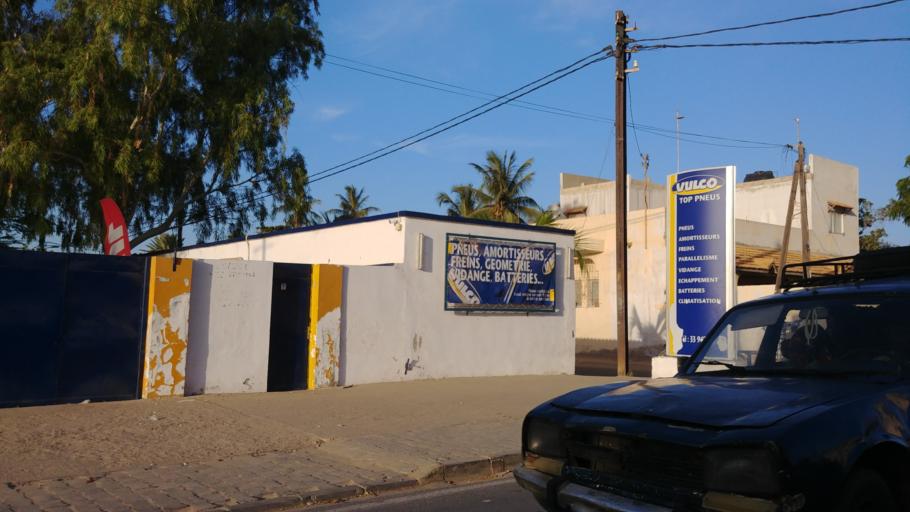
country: SN
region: Saint-Louis
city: Saint-Louis
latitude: 16.0257
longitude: -16.4859
